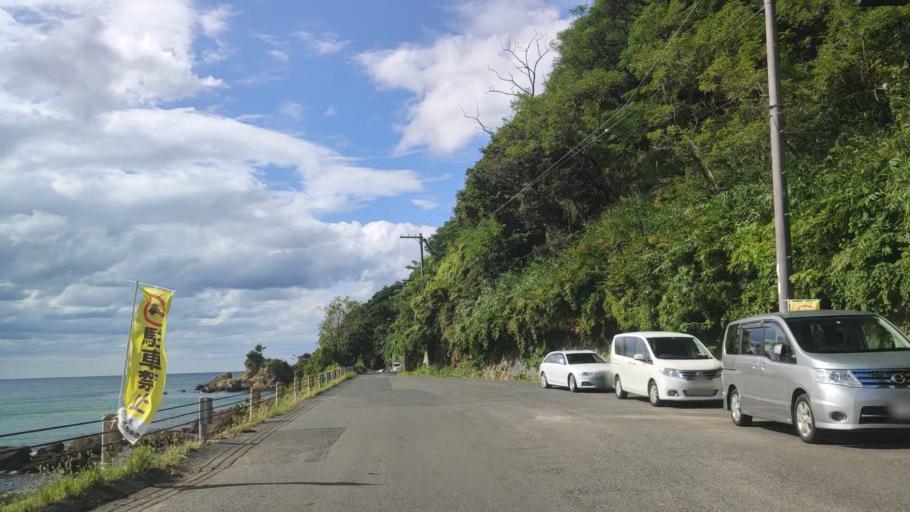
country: JP
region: Hyogo
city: Toyooka
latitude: 35.6697
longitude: 134.9671
